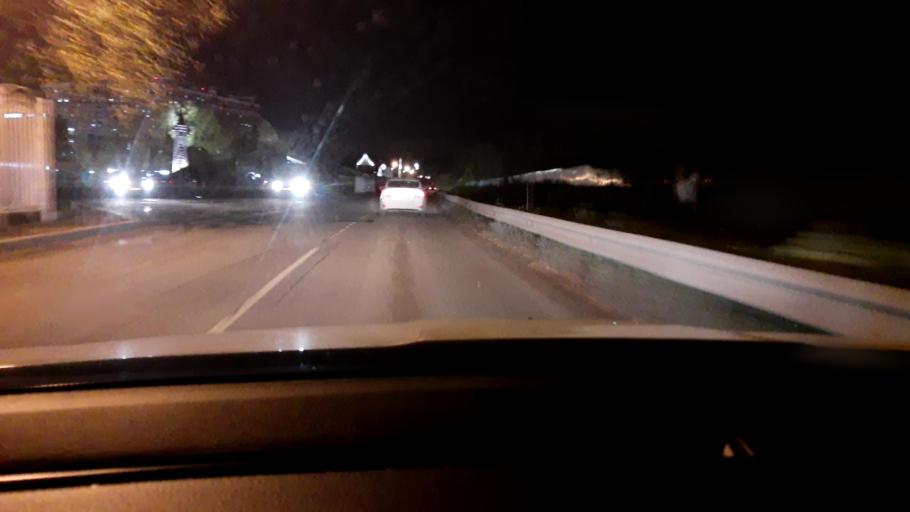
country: RU
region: Moskovskaya
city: Razvilka
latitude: 55.5816
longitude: 37.7344
